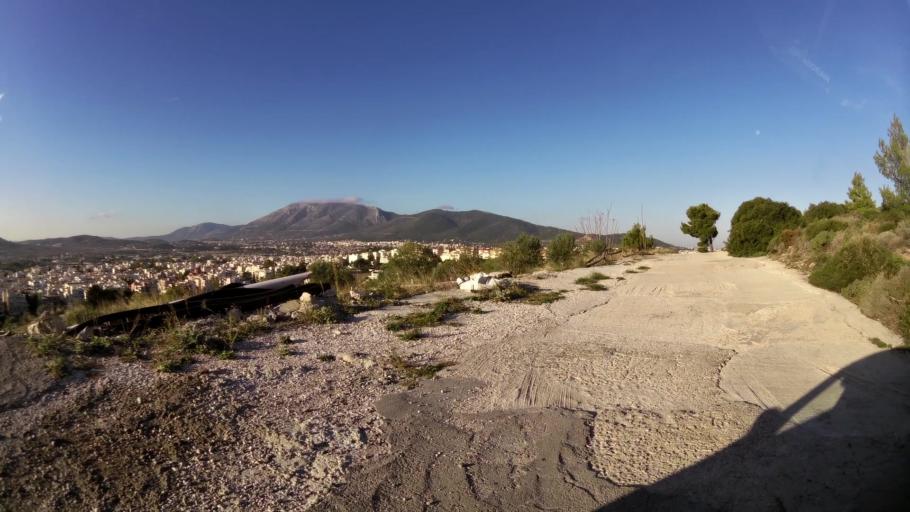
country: GR
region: Attica
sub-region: Nomarchia Anatolikis Attikis
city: Pallini
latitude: 38.0099
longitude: 23.8851
